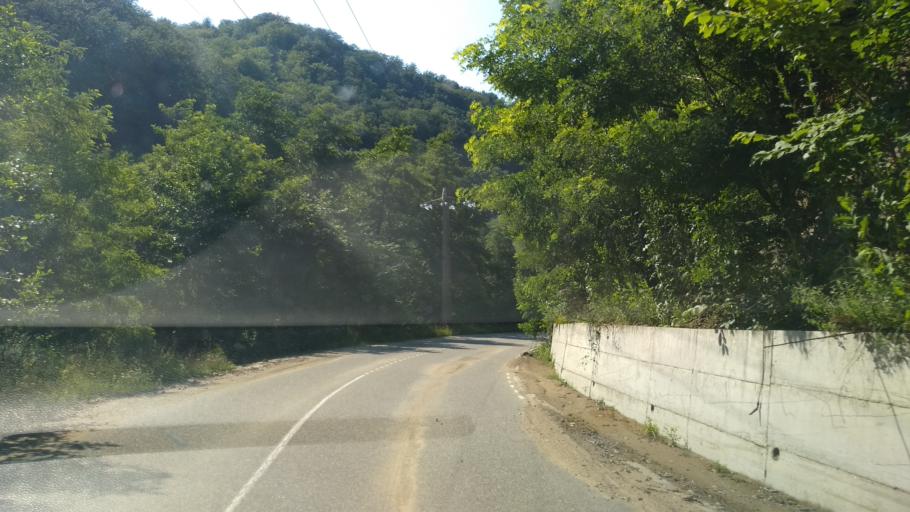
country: RO
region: Hunedoara
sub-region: Comuna Orastioara de Sus
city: Orastioara de Sus
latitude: 45.6712
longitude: 23.1698
